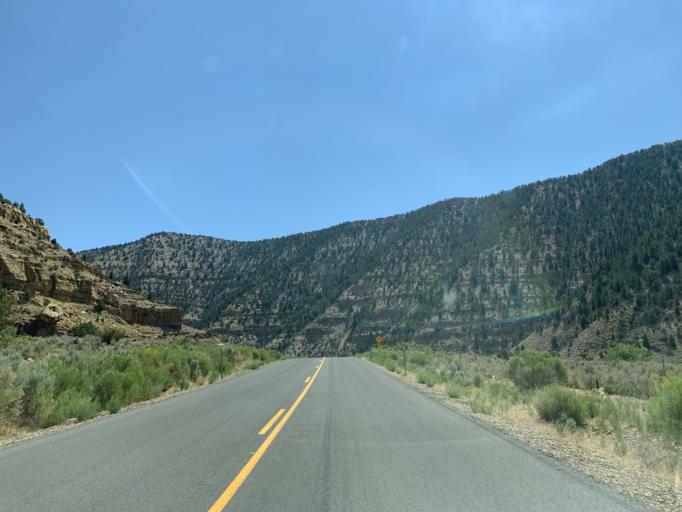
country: US
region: Utah
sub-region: Carbon County
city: East Carbon City
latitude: 39.7854
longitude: -110.4022
